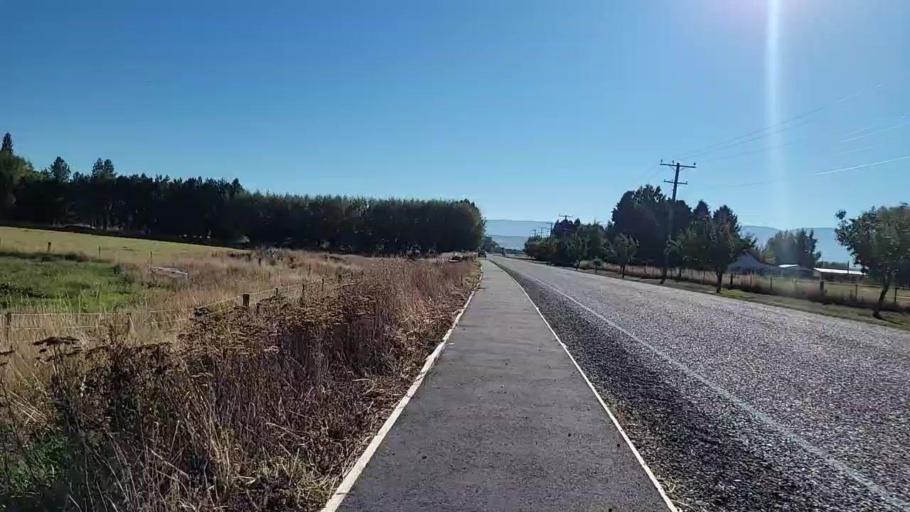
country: NZ
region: Otago
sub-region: Queenstown-Lakes District
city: Wanaka
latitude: -45.0042
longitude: 169.9157
